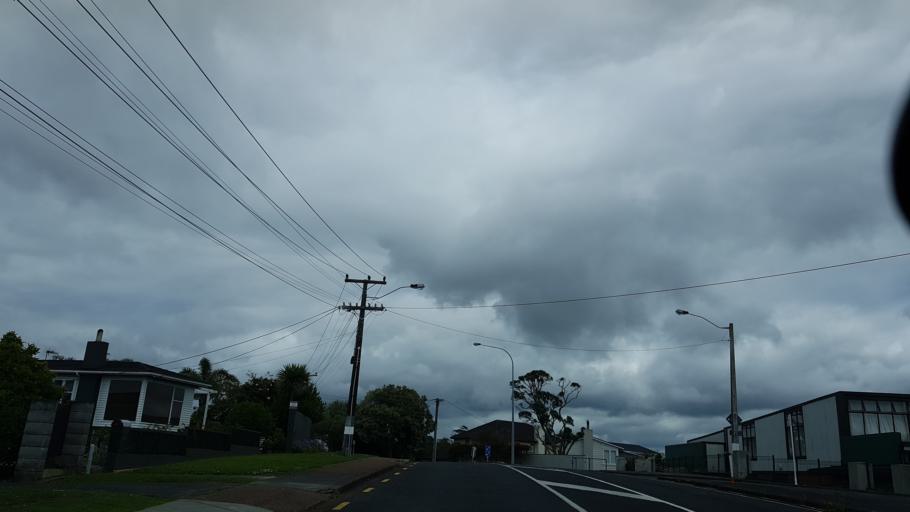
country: NZ
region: Auckland
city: Murrays Bay
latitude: -36.7347
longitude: 174.7446
